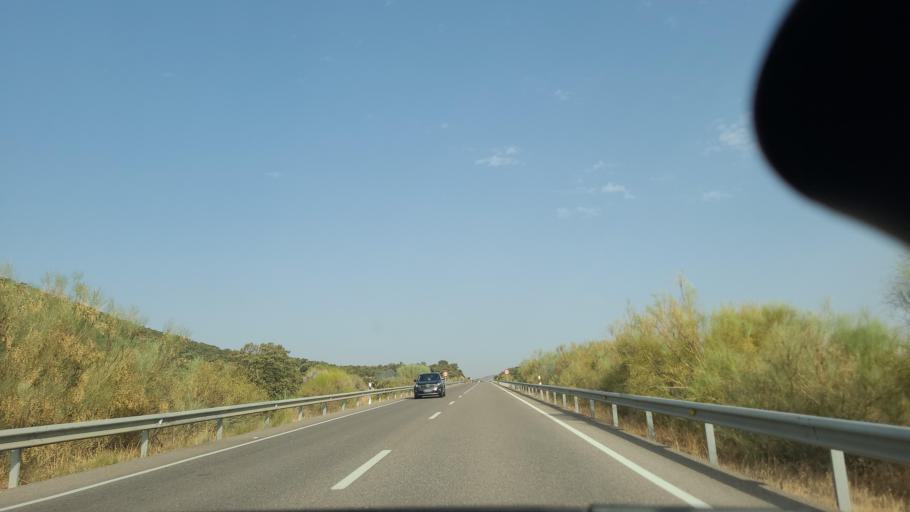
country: ES
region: Andalusia
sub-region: Province of Cordoba
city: Belmez
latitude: 38.2237
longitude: -5.1572
